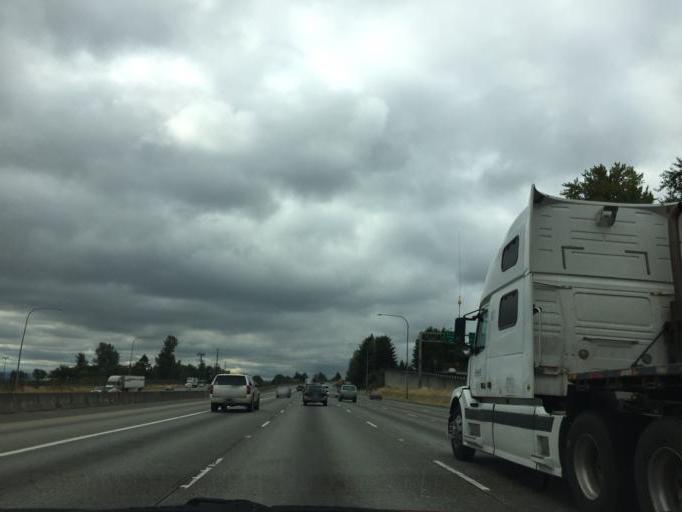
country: US
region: Washington
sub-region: King County
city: SeaTac
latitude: 47.4364
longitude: -122.2698
